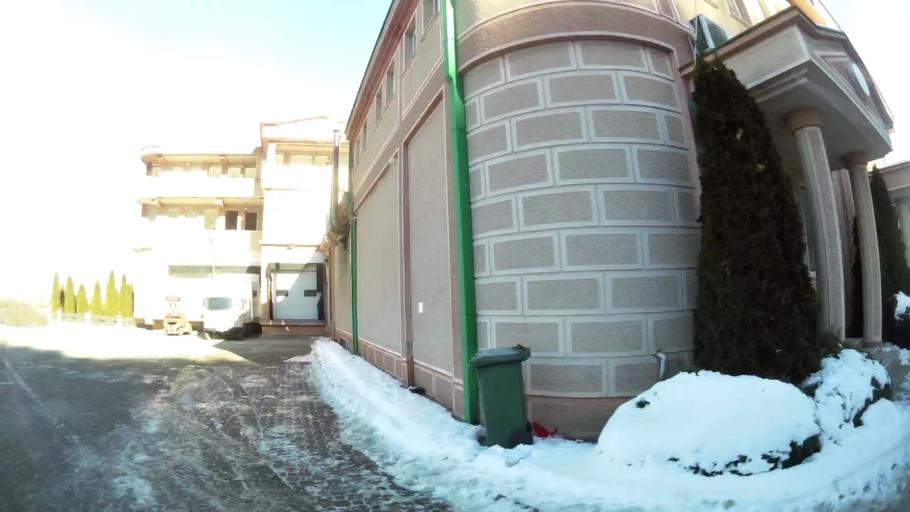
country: MK
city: Ljubin
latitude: 42.0030
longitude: 21.3000
